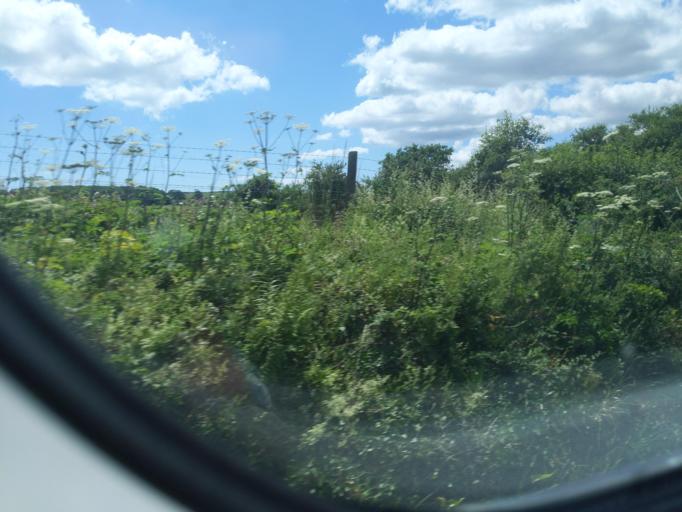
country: GB
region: England
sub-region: Cornwall
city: Pillaton
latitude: 50.4196
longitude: -4.3818
